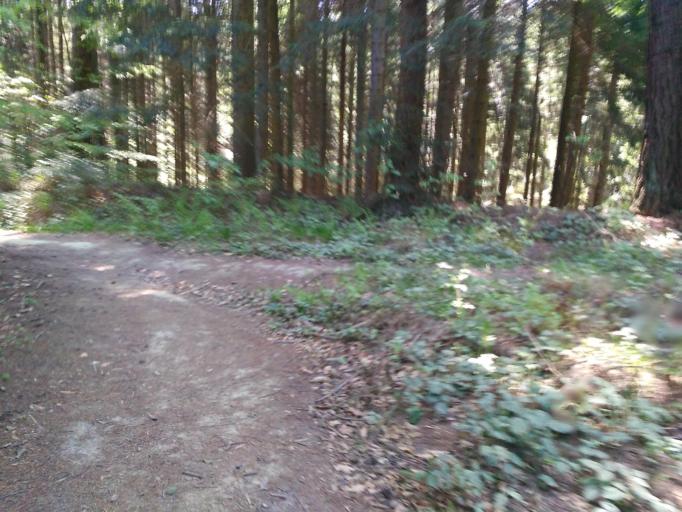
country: PL
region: Subcarpathian Voivodeship
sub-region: Powiat krosnienski
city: Korczyna
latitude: 49.7350
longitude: 21.8583
